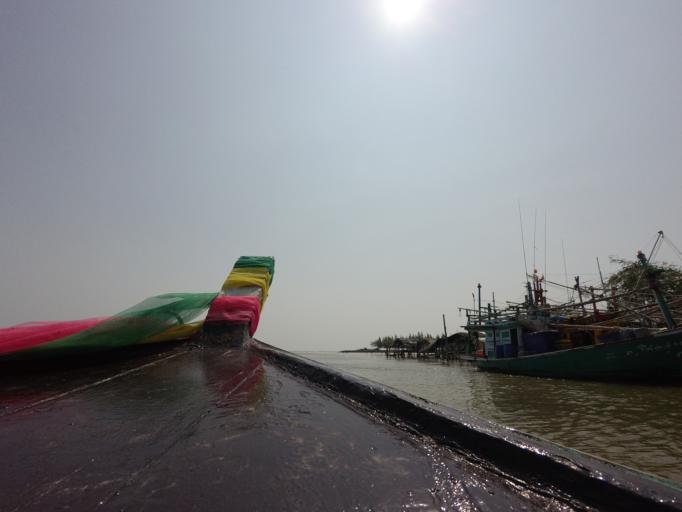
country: TH
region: Prachuap Khiri Khan
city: Kui Buri
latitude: 12.1337
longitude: 99.9682
